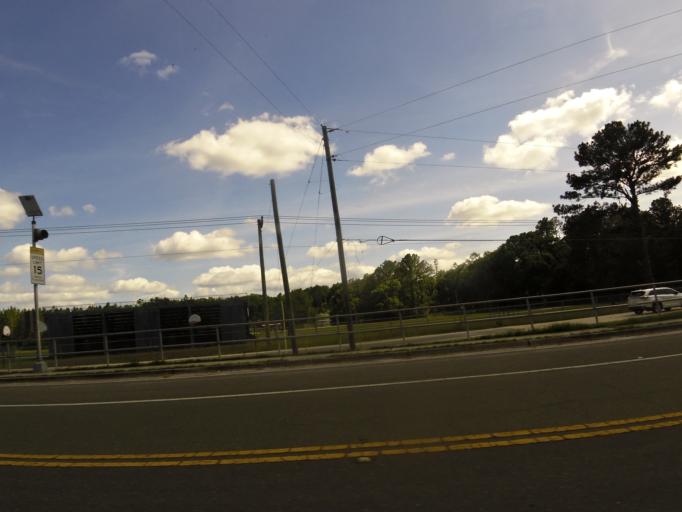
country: US
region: Florida
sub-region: Nassau County
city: Callahan
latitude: 30.5708
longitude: -81.8418
